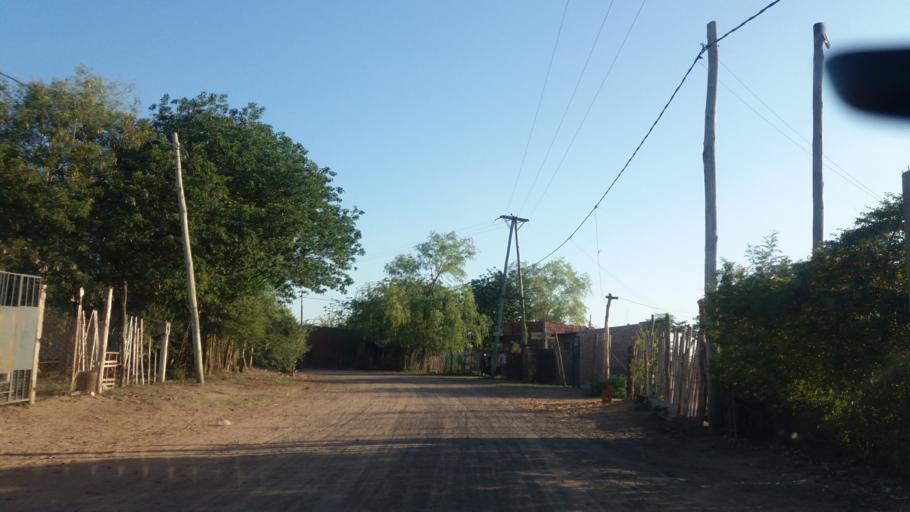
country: AR
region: Corrientes
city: Corrientes
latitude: -27.5174
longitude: -58.8298
